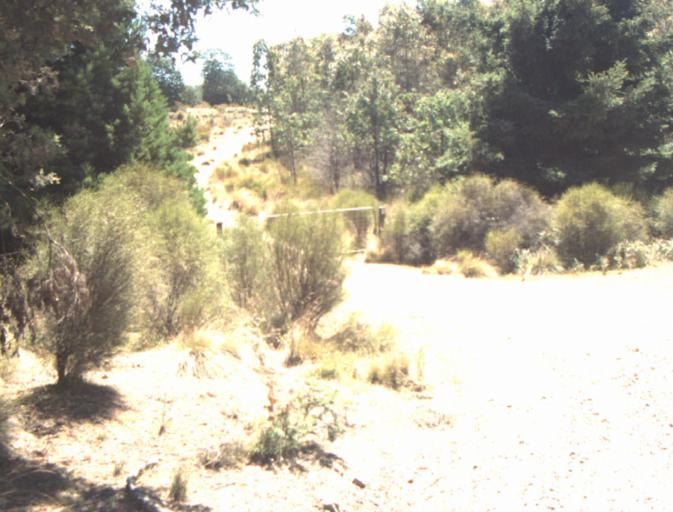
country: AU
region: Tasmania
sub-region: Dorset
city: Scottsdale
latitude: -41.3095
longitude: 147.4655
